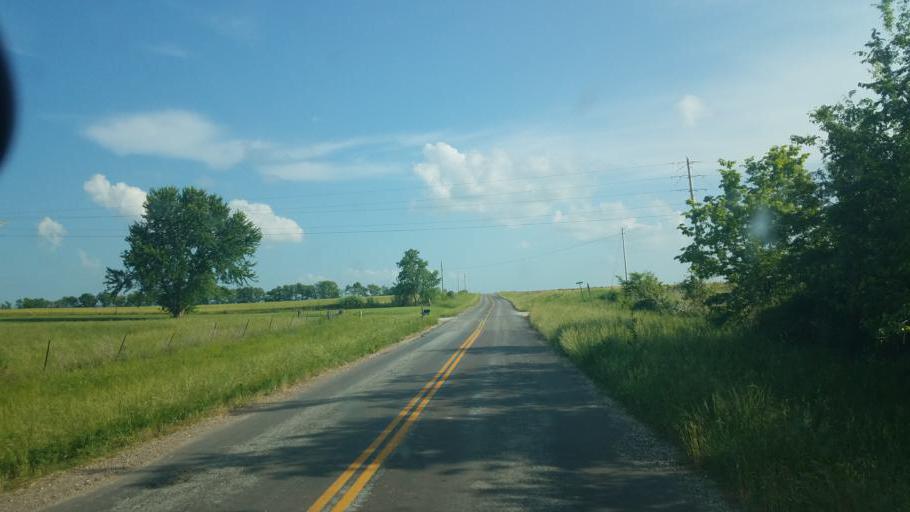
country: US
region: Missouri
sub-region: Moniteau County
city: California
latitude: 38.7977
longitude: -92.6049
